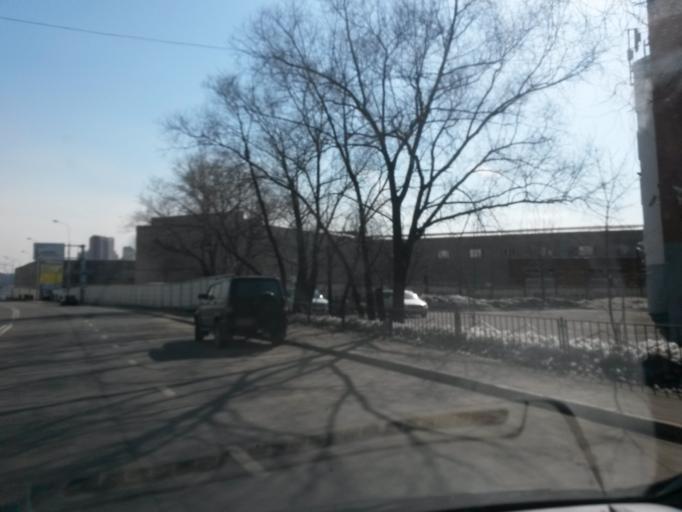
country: RU
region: Moskovskaya
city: Shcherbinka
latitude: 55.5371
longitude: 37.5756
